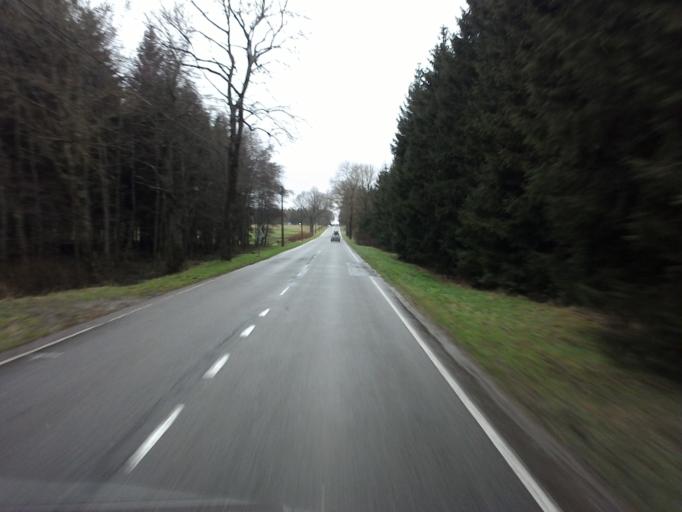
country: BE
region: Wallonia
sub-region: Province de Liege
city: Stavelot
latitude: 50.4228
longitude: 5.9318
